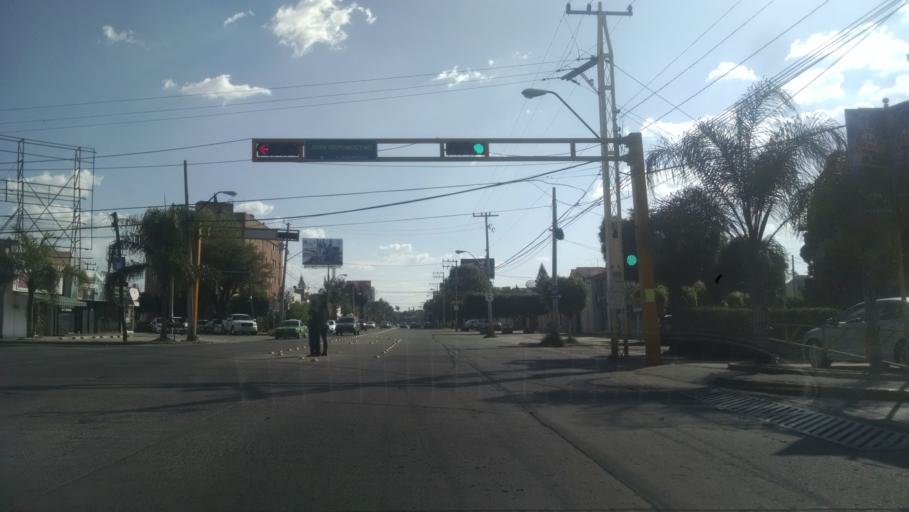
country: MX
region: Guanajuato
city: Leon
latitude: 21.1531
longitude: -101.6889
